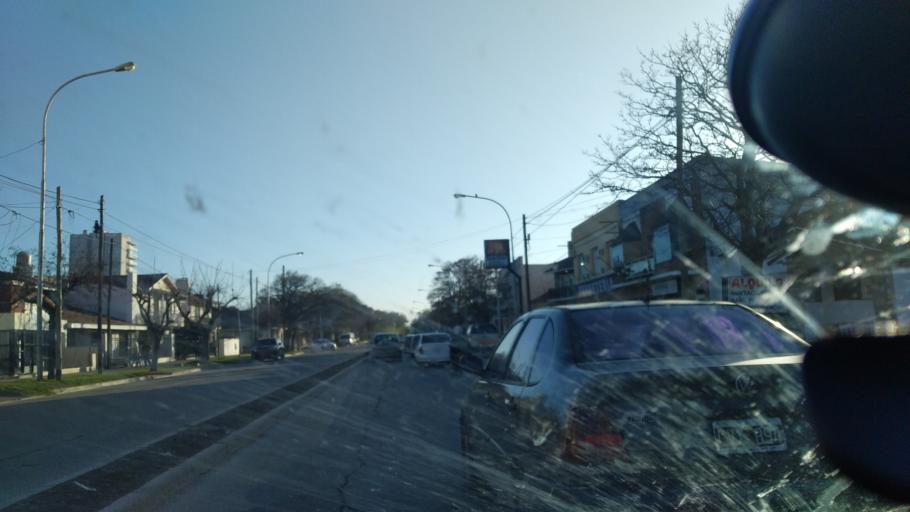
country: AR
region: Buenos Aires
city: Necochea
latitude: -38.5786
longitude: -58.7319
